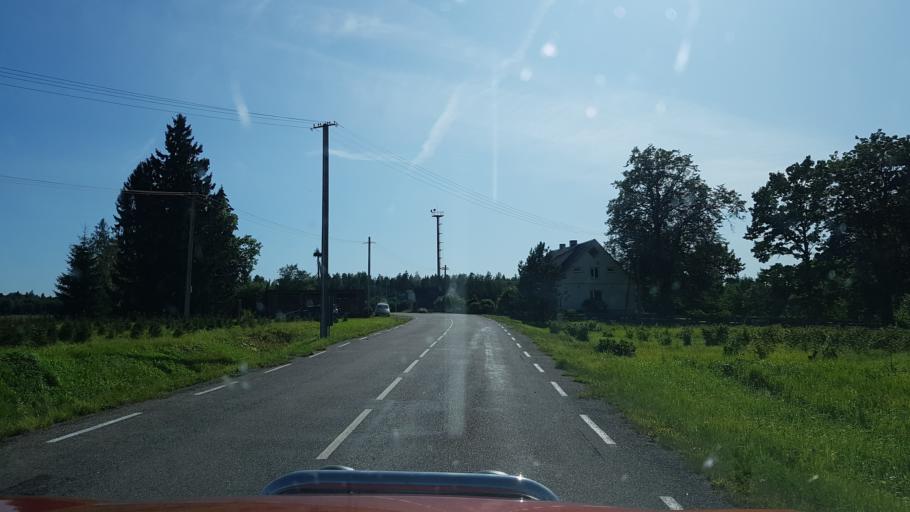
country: EE
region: Paernumaa
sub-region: Saarde vald
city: Kilingi-Nomme
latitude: 58.0217
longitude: 25.0085
